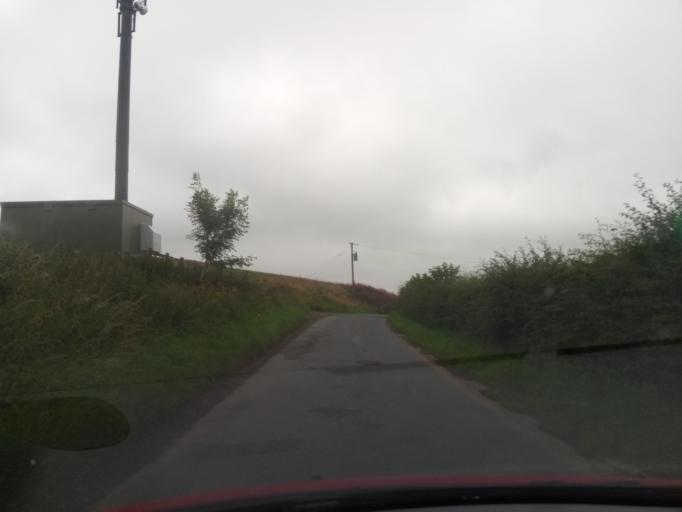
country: GB
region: Scotland
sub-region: Fife
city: Pathhead
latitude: 55.7740
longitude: -2.9520
